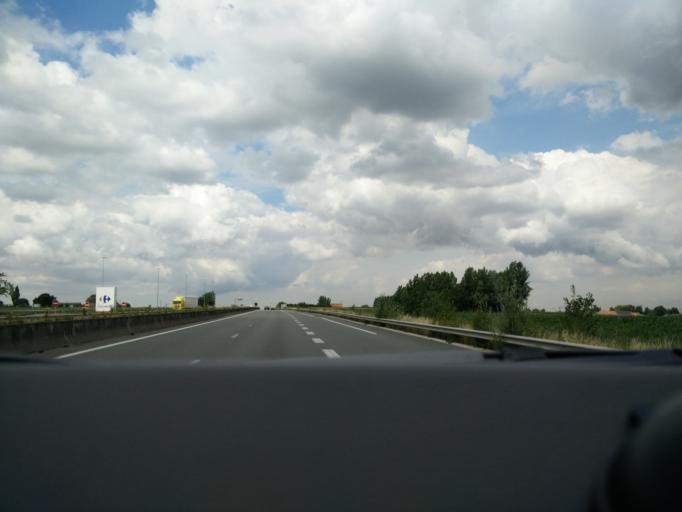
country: FR
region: Nord-Pas-de-Calais
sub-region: Departement du Nord
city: Steenvoorde
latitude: 50.8307
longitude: 2.5809
